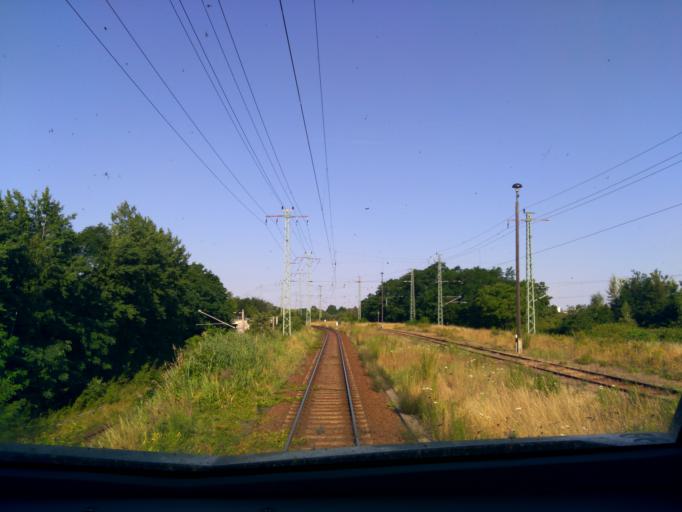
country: DE
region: Brandenburg
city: Cottbus
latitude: 51.7513
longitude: 14.3089
